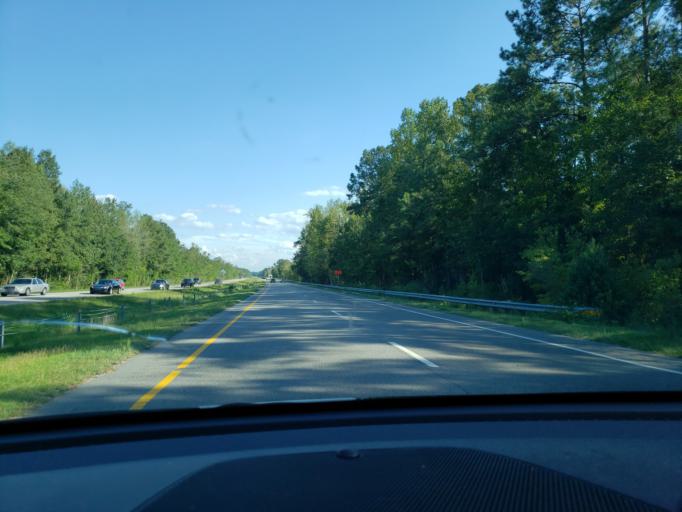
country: US
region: North Carolina
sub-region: Robeson County
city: Fairmont
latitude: 34.4760
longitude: -78.9856
